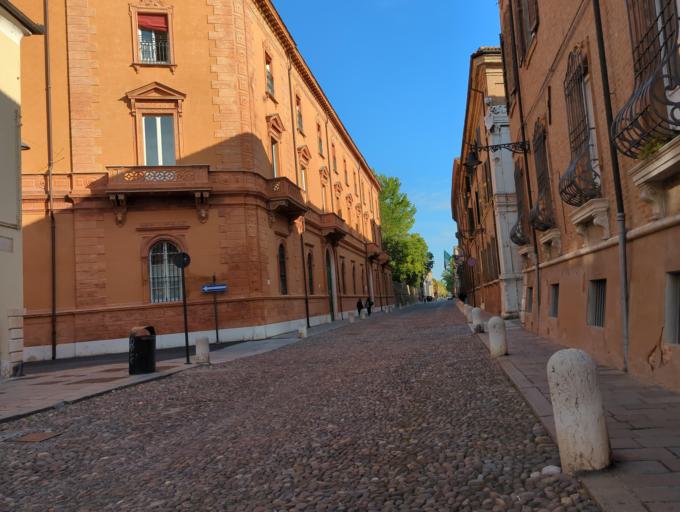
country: IT
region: Emilia-Romagna
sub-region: Provincia di Ferrara
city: Ferrara
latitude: 44.8400
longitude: 11.6206
